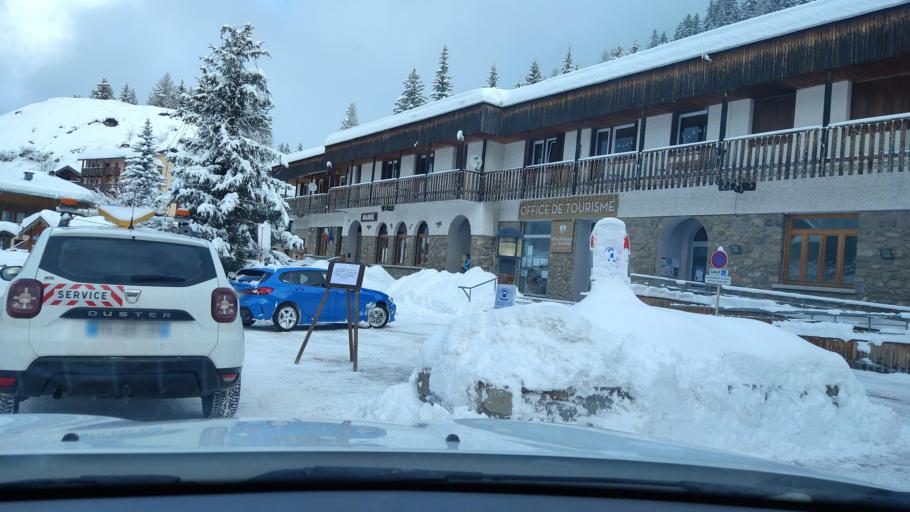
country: FR
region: Rhone-Alpes
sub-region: Departement de la Savoie
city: Courchevel
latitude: 45.3817
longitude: 6.7213
